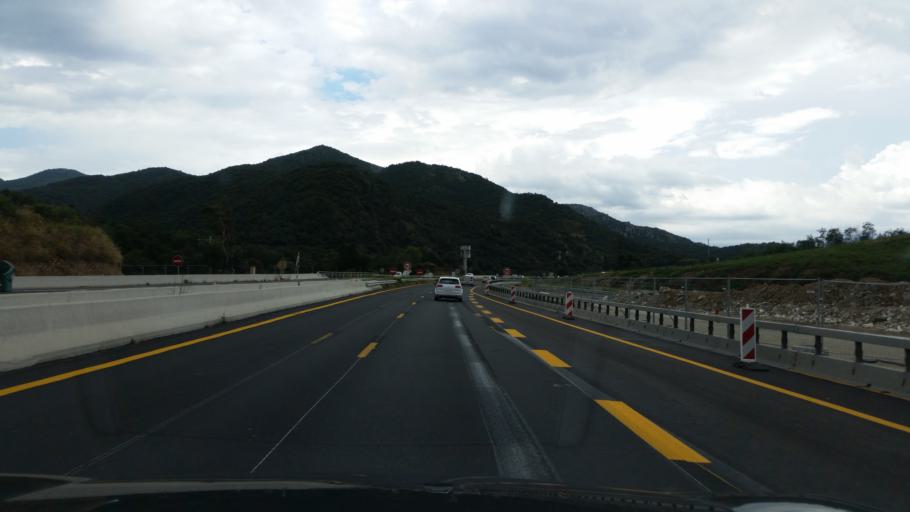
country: FR
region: Languedoc-Roussillon
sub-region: Departement des Pyrenees-Orientales
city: Montesquiu d'Albera
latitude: 42.4727
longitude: 2.8619
